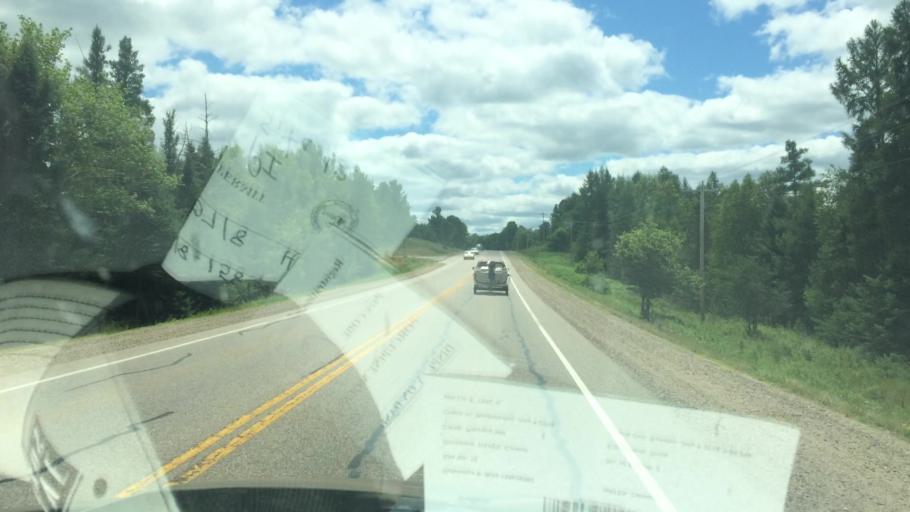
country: US
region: Wisconsin
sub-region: Vilas County
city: Eagle River
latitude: 45.7975
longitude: -89.3202
